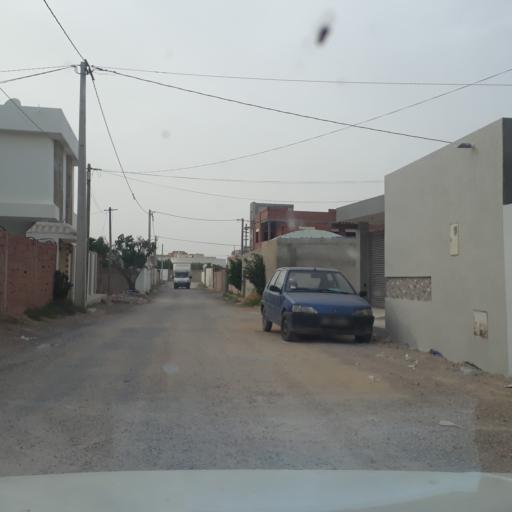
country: TN
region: Safaqis
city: Al Qarmadah
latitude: 34.8215
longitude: 10.7744
